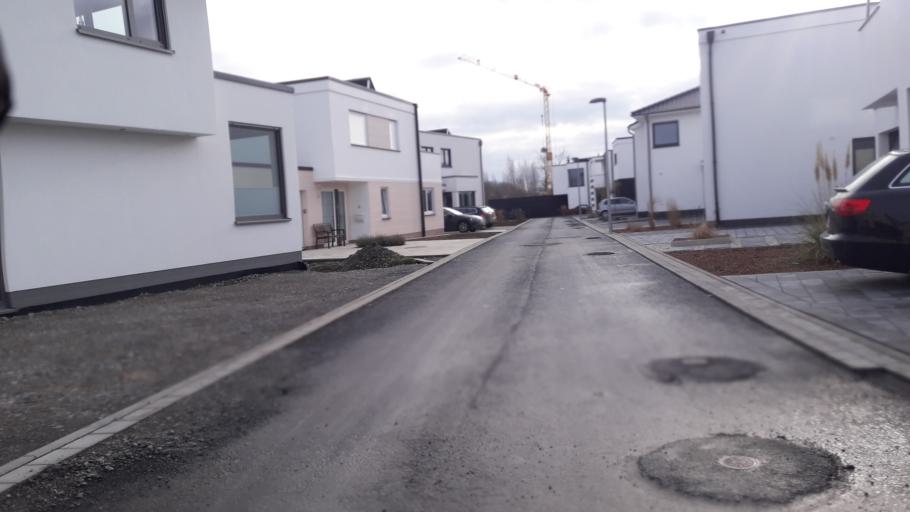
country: DE
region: North Rhine-Westphalia
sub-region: Regierungsbezirk Arnsberg
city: Soest
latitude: 51.5842
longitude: 8.1019
